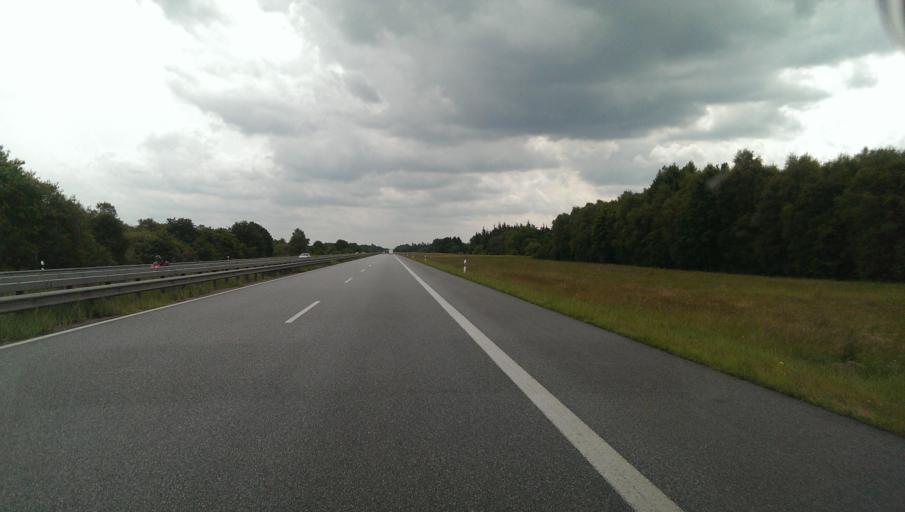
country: DE
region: Lower Saxony
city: Uthlede
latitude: 53.3513
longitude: 8.5949
